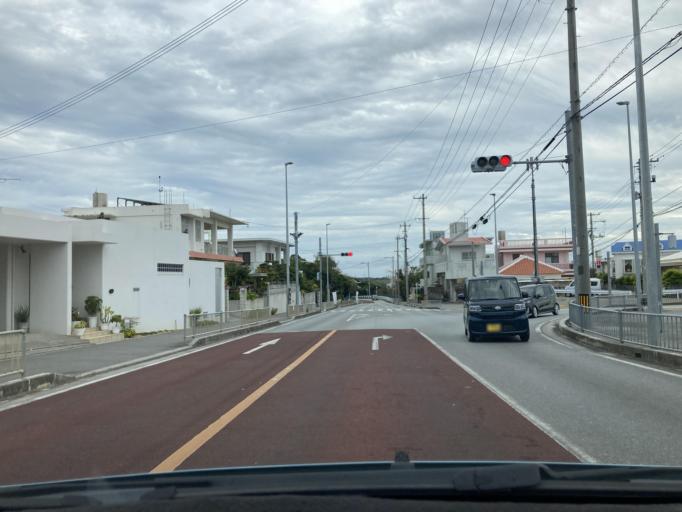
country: JP
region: Okinawa
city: Ishikawa
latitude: 26.4028
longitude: 127.7389
